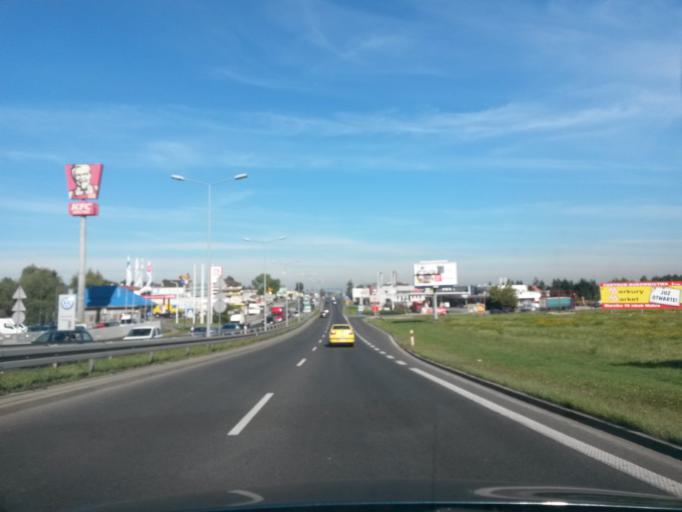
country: PL
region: Lesser Poland Voivodeship
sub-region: Powiat krakowski
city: Libertow
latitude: 49.9799
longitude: 19.9107
